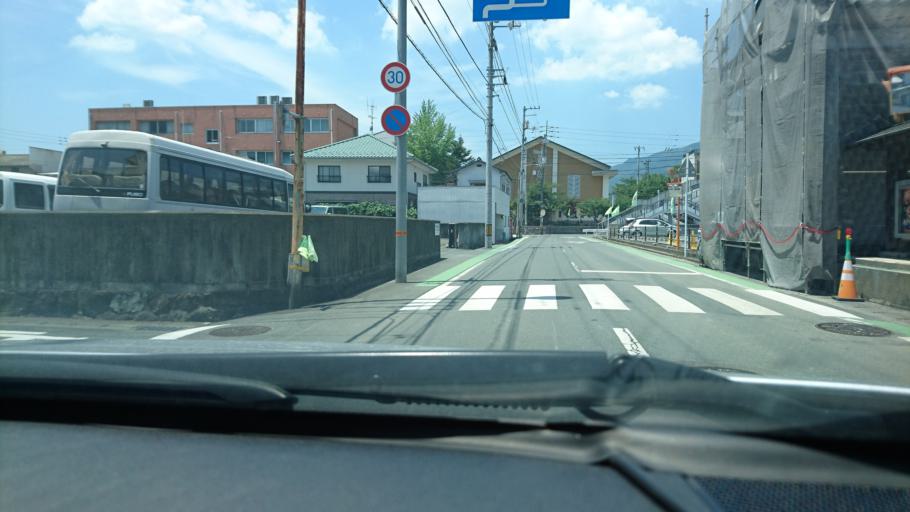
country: JP
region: Ehime
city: Ozu
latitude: 33.5068
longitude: 132.5434
